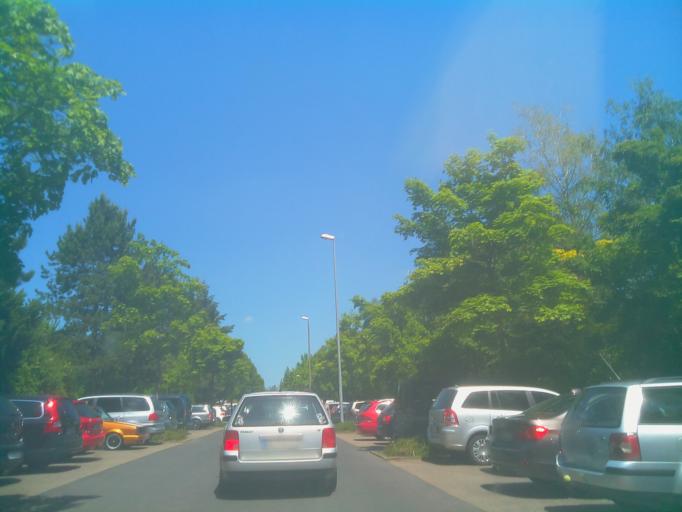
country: DE
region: Bavaria
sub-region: Regierungsbezirk Unterfranken
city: Sennfeld
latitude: 50.0656
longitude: 10.2475
